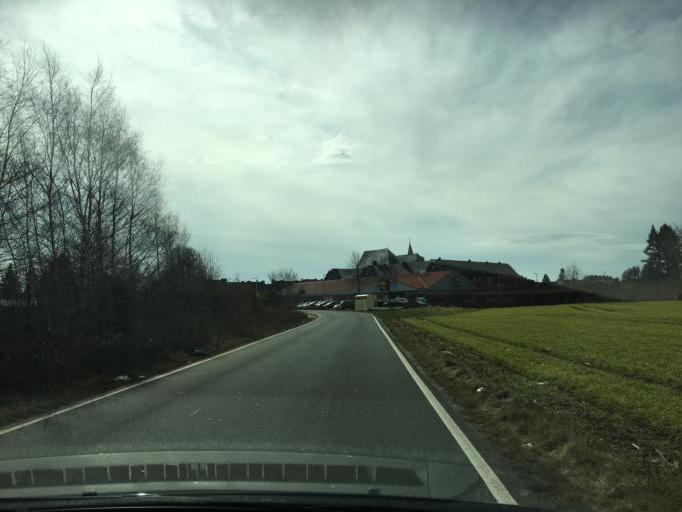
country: DE
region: North Rhine-Westphalia
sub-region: Regierungsbezirk Koln
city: Dueren
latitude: 50.8125
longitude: 6.5089
